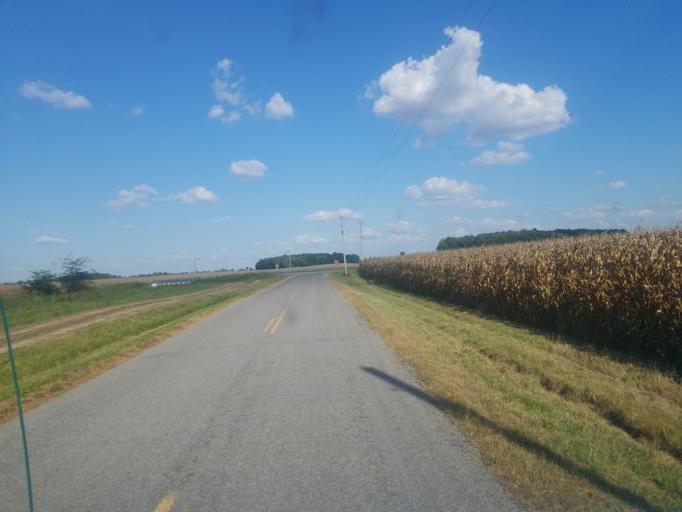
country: US
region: Ohio
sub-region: Logan County
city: Northwood
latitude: 40.4668
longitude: -83.5801
